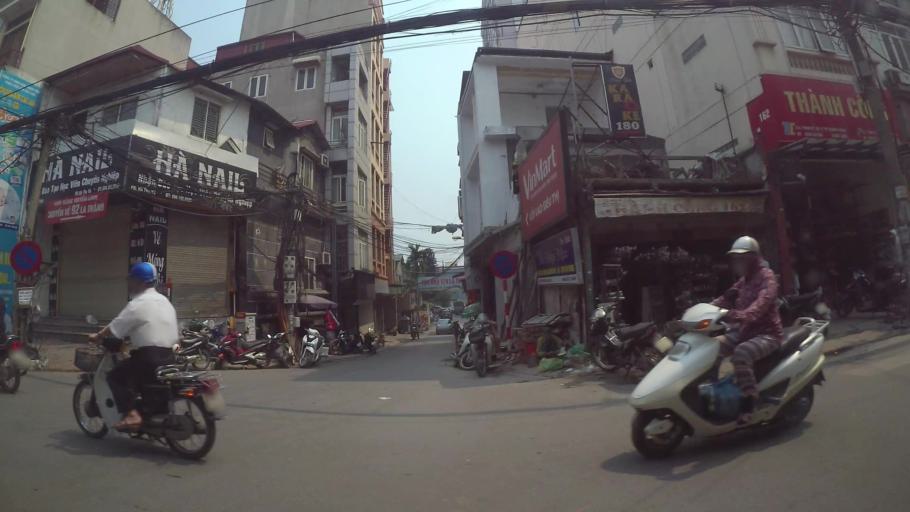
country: VN
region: Ha Noi
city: Dong Da
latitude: 21.0205
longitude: 105.8273
